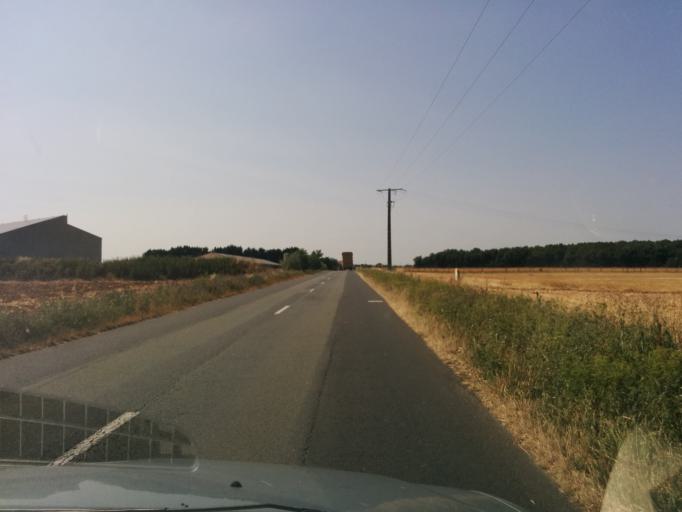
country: FR
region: Poitou-Charentes
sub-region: Departement de la Vienne
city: Mirebeau
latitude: 46.7387
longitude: 0.1855
